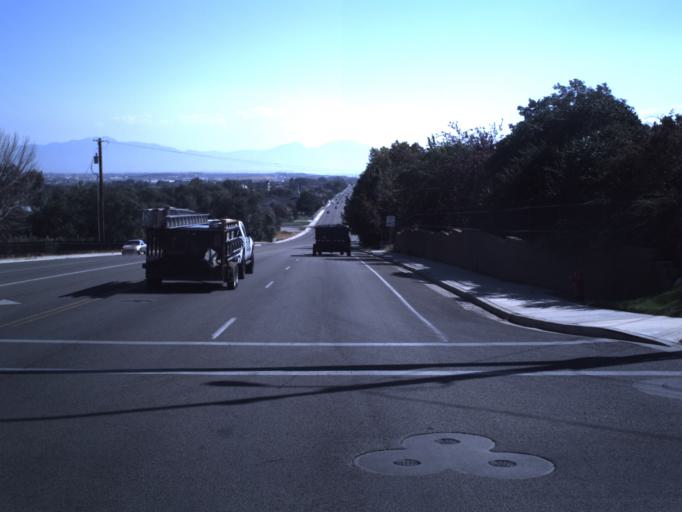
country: US
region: Utah
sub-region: Utah County
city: Cedar Hills
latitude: 40.3919
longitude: -111.7692
